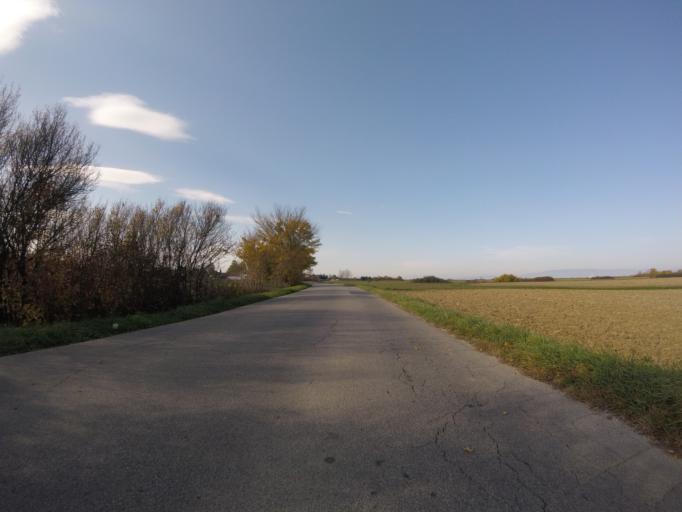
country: HR
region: Zagrebacka
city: Mraclin
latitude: 45.6696
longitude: 16.1098
